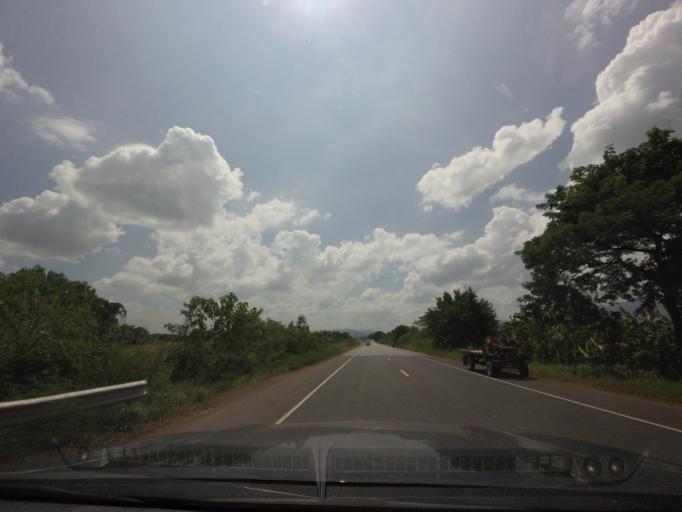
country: TH
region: Phetchabun
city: Phetchabun
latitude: 16.4499
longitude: 101.1130
